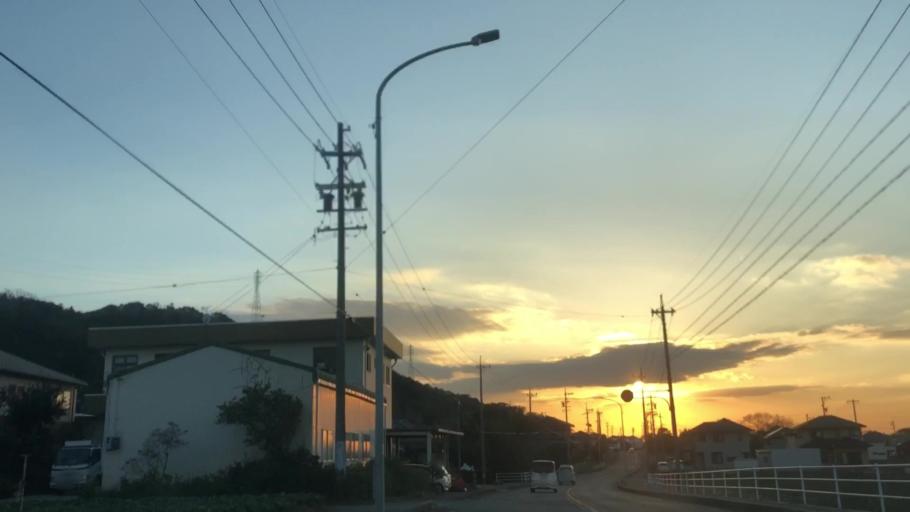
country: JP
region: Aichi
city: Toyohama
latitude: 34.6059
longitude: 137.0660
